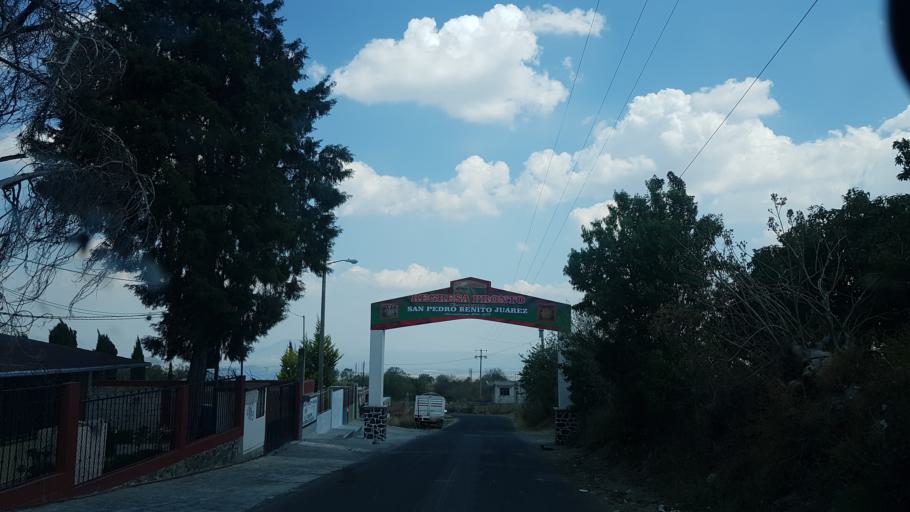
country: MX
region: Puebla
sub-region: Atlixco
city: San Pedro Benito Juarez
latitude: 18.9494
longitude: -98.5410
